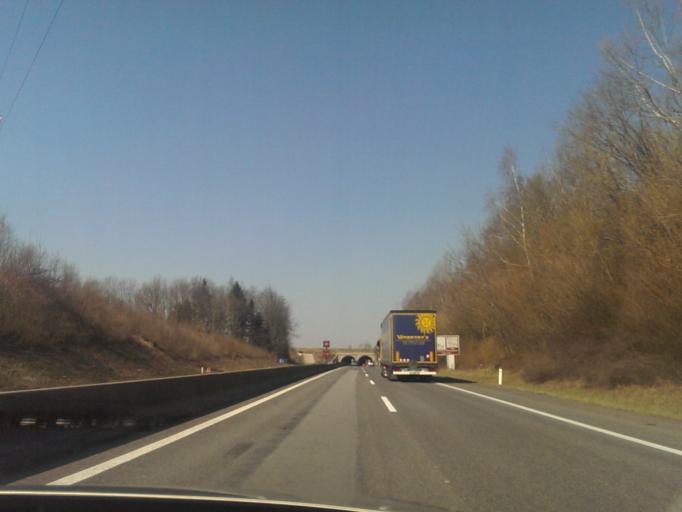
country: AT
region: Upper Austria
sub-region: Politischer Bezirk Kirchdorf an der Krems
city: Kremsmunster
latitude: 47.9984
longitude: 14.0826
